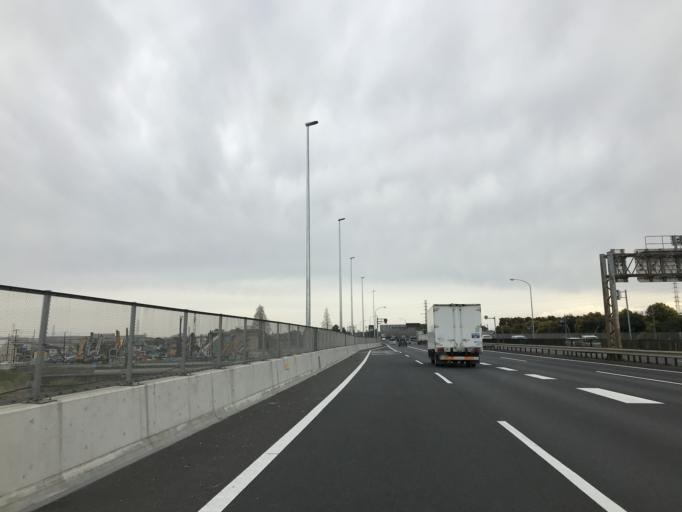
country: JP
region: Saitama
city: Yashio-shi
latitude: 35.8406
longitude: 139.8644
